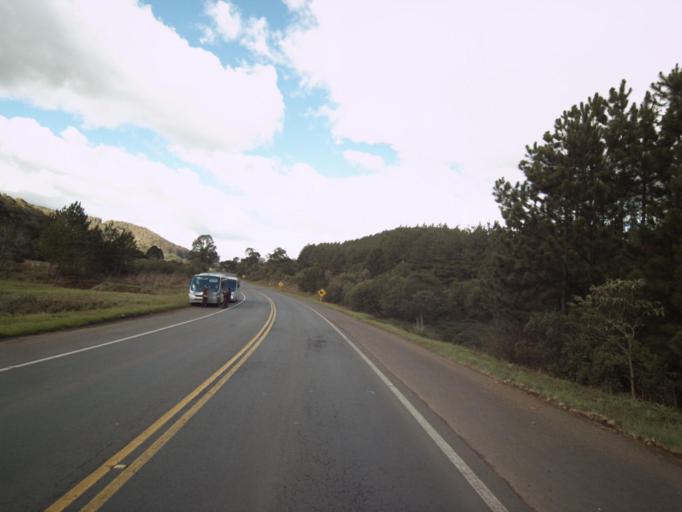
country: BR
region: Santa Catarina
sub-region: Joacaba
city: Joacaba
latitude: -27.0542
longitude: -51.6975
